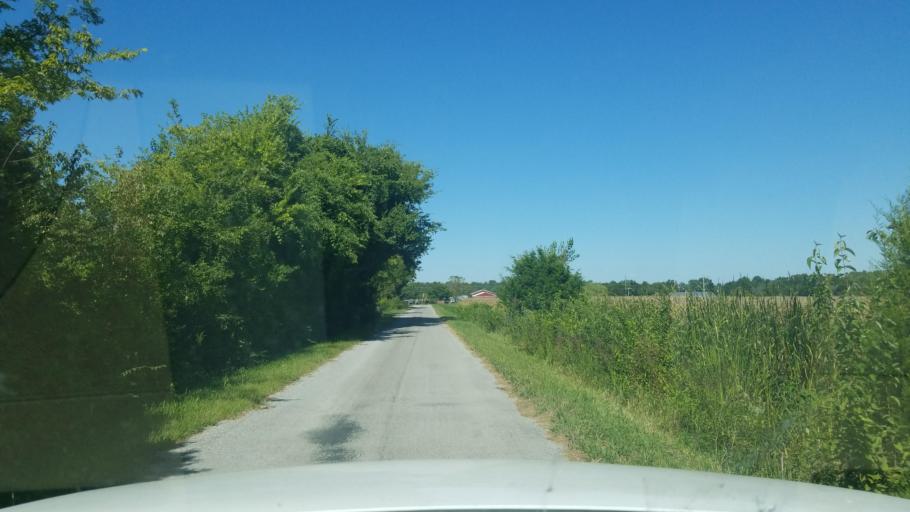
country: US
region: Illinois
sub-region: Saline County
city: Eldorado
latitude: 37.8595
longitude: -88.5119
